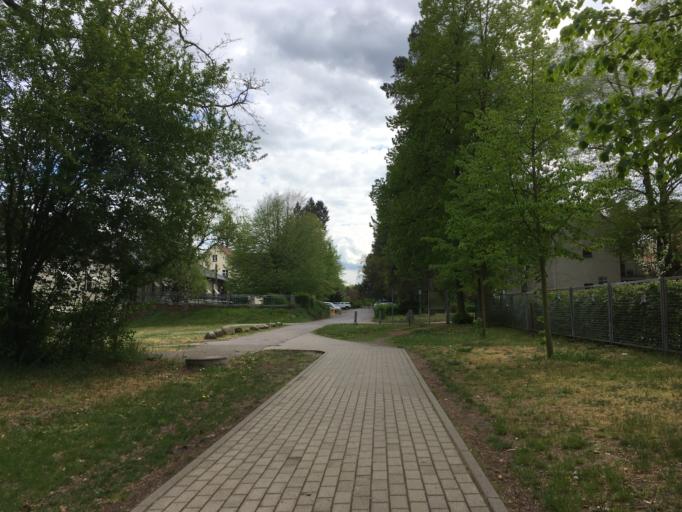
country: DE
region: Brandenburg
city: Rudnitz
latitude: 52.7293
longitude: 13.5973
